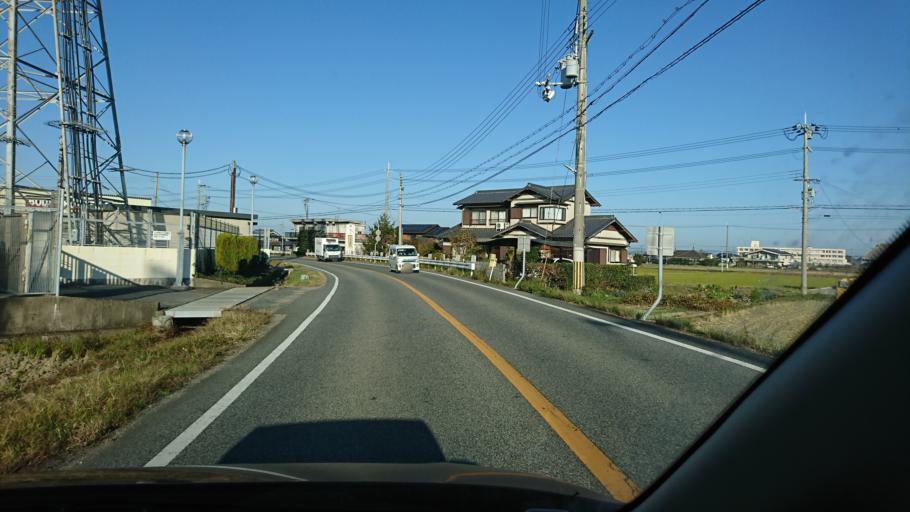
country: JP
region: Hyogo
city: Miki
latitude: 34.7336
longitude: 134.9215
